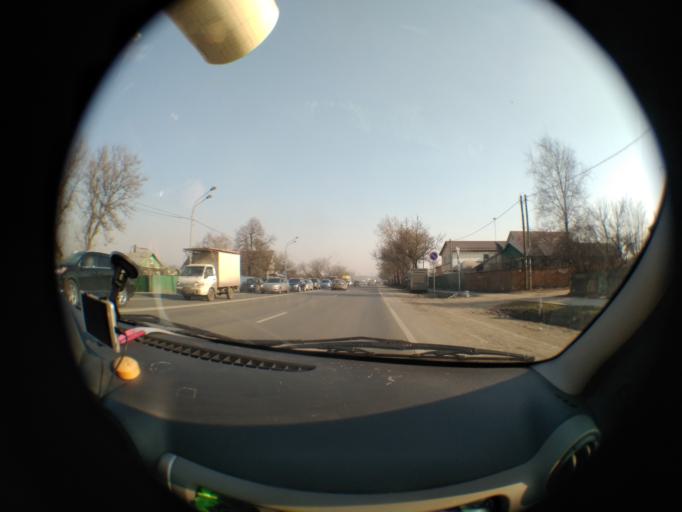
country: RU
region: Moskovskaya
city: Ostrovtsy
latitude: 55.5869
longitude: 38.0094
